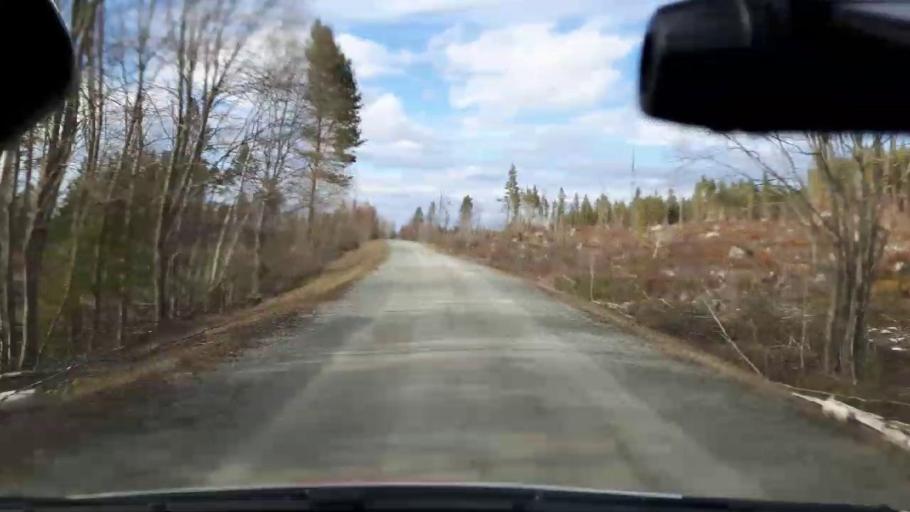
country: SE
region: Jaemtland
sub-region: Bergs Kommun
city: Hoverberg
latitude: 62.7393
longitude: 14.6636
